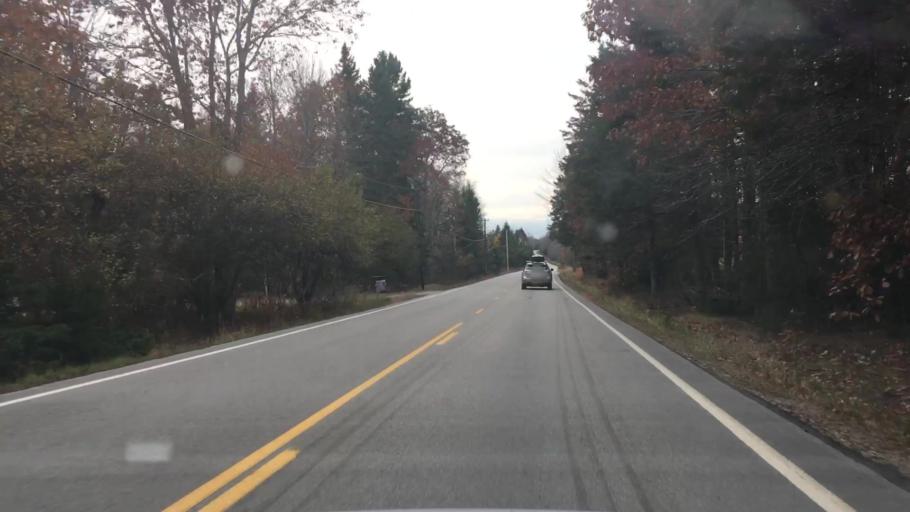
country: US
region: Maine
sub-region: Hancock County
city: Penobscot
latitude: 44.4765
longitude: -68.6377
